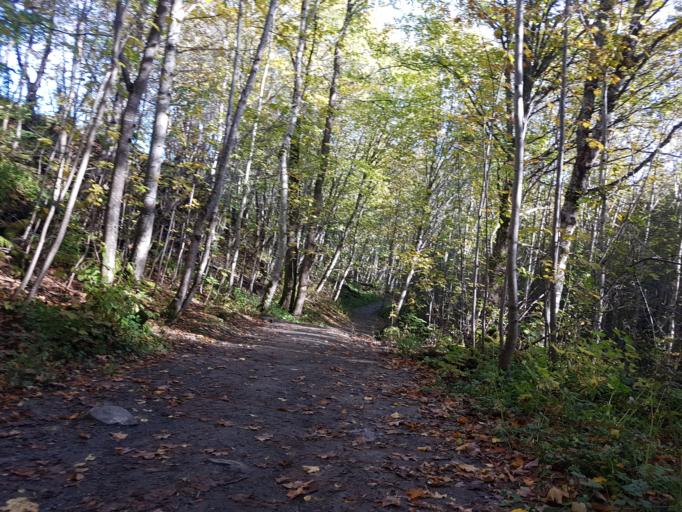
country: NO
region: Sor-Trondelag
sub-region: Trondheim
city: Trondheim
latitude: 63.4257
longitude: 10.3552
